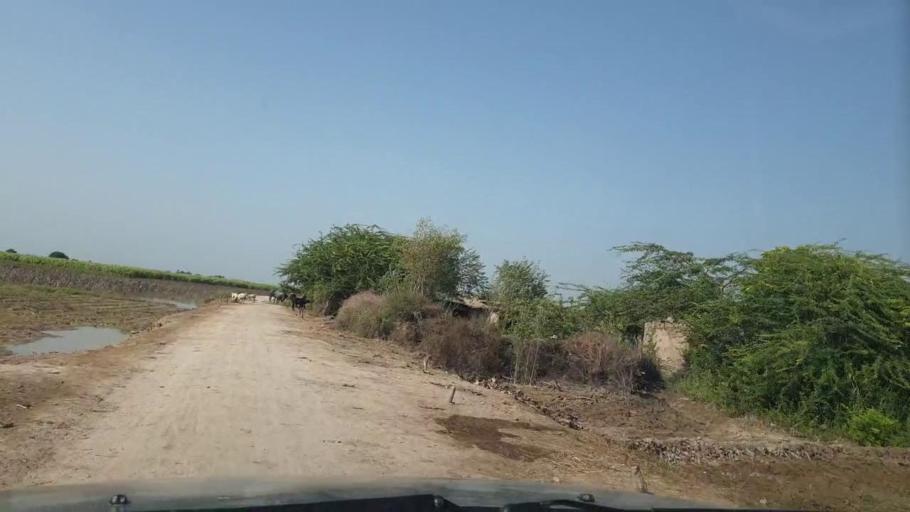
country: PK
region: Sindh
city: Chambar
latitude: 25.2527
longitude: 68.9052
